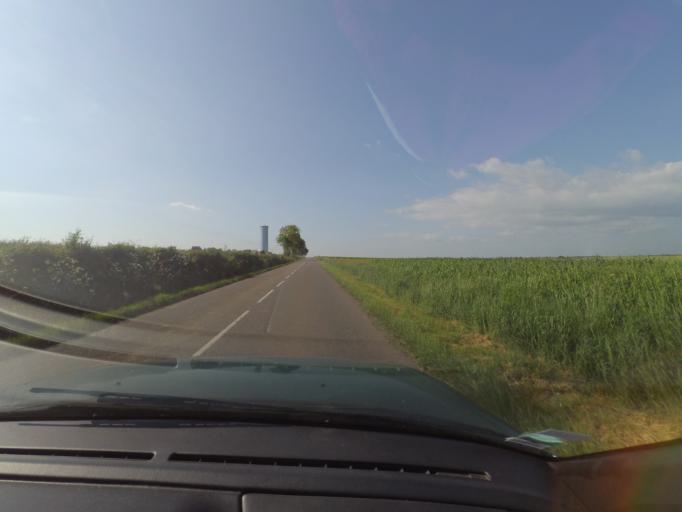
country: FR
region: Pays de la Loire
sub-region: Departement de la Vendee
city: Angles
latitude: 46.4103
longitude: -1.3851
